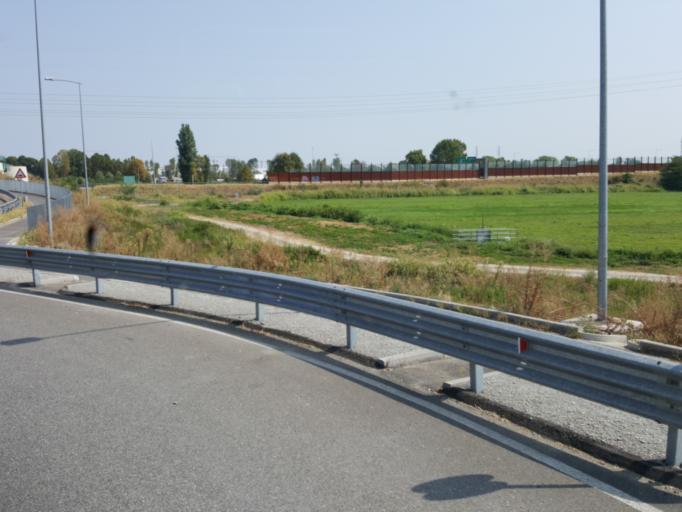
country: IT
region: Lombardy
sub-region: Citta metropolitana di Milano
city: Pozzuolo Martesana
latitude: 45.5114
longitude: 9.4377
